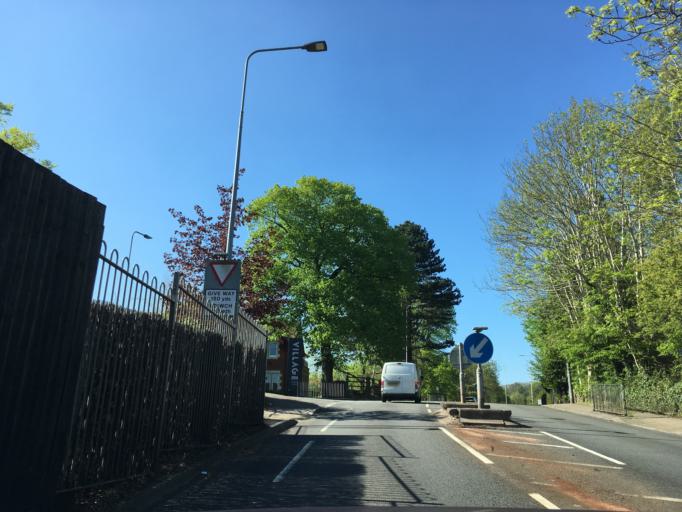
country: GB
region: Wales
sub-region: Cardiff
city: Radyr
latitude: 51.5239
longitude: -3.2375
